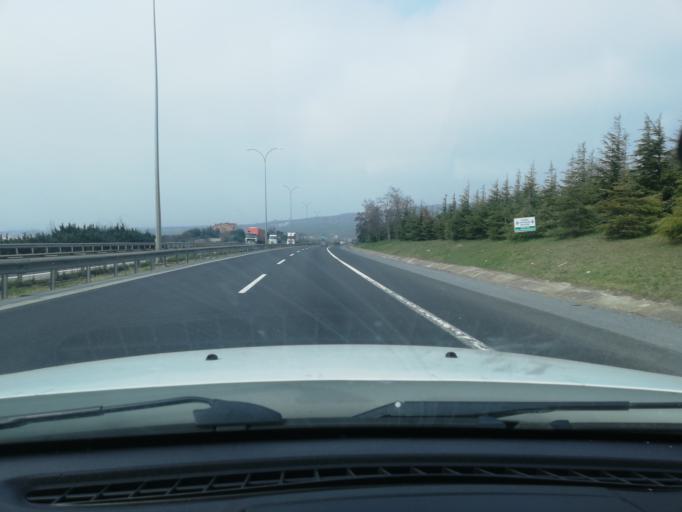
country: TR
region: Istanbul
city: Celaliye
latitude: 41.0597
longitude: 28.4118
